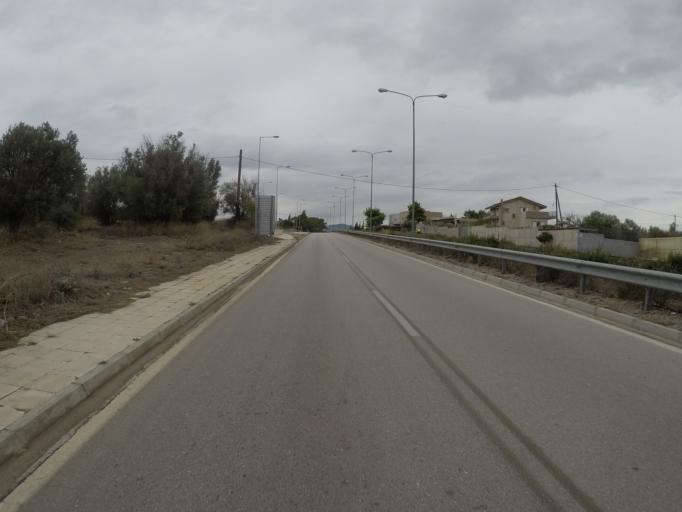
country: GR
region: Peloponnese
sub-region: Nomos Korinthias
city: Korinthos
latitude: 37.9439
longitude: 22.9792
